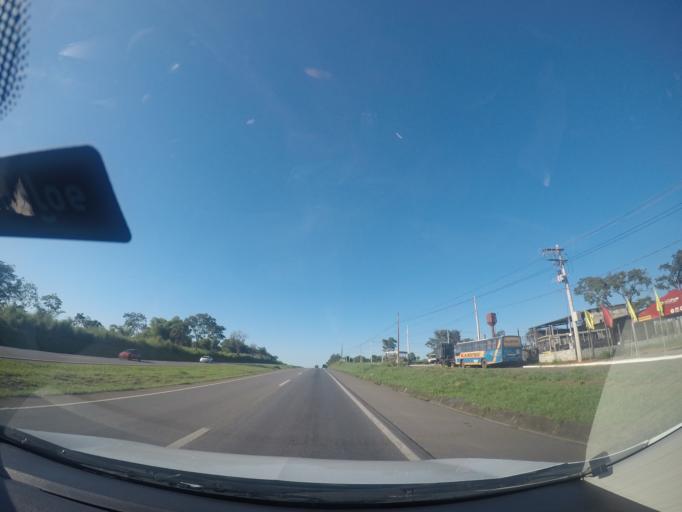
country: BR
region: Goias
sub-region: Aparecida De Goiania
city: Aparecida de Goiania
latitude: -16.8623
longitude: -49.2496
